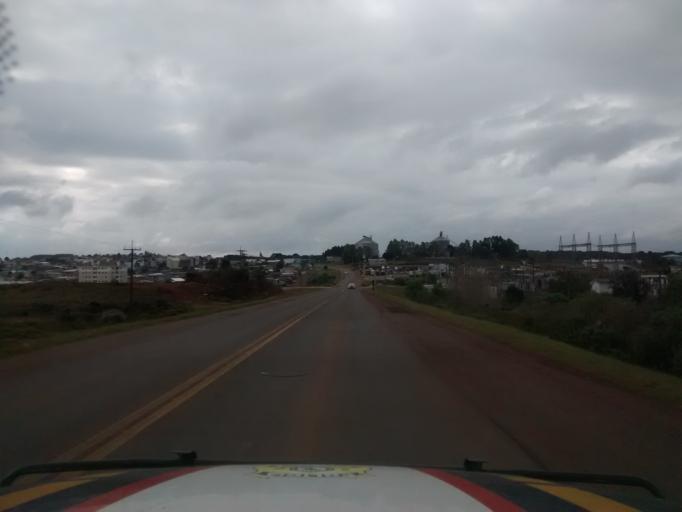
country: BR
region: Rio Grande do Sul
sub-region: Lagoa Vermelha
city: Lagoa Vermelha
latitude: -28.2179
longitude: -51.5098
